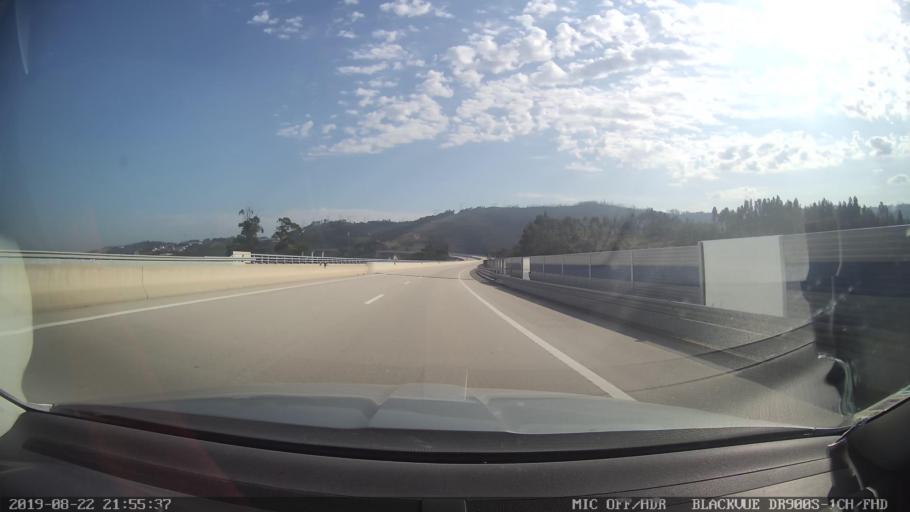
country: PT
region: Coimbra
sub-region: Coimbra
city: Coimbra
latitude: 40.1560
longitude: -8.3843
